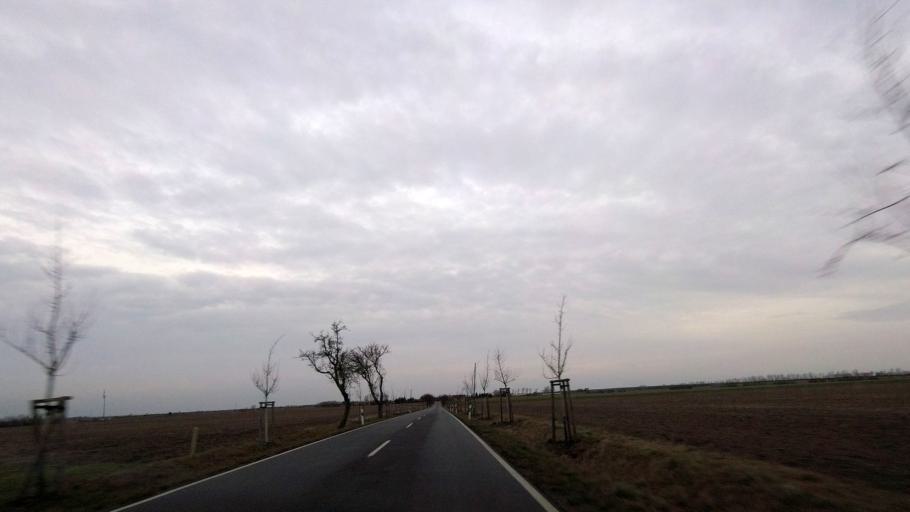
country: DE
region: Brandenburg
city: Niedergorsdorf
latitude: 51.9446
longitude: 12.9782
